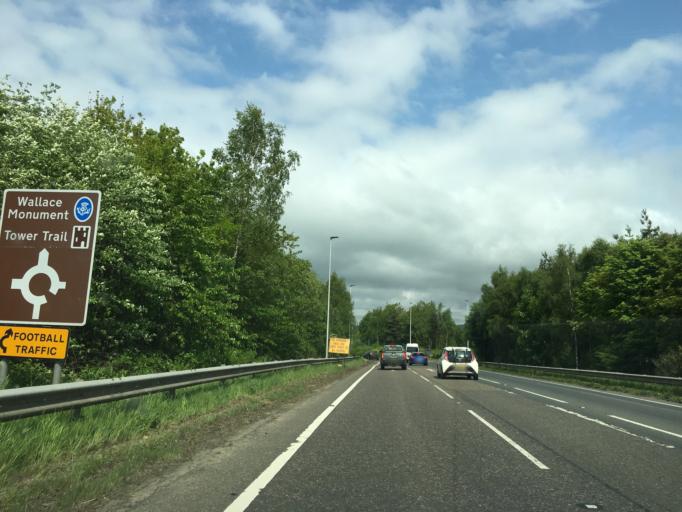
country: GB
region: Scotland
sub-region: Stirling
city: Bannockburn
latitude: 56.1077
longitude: -3.9056
